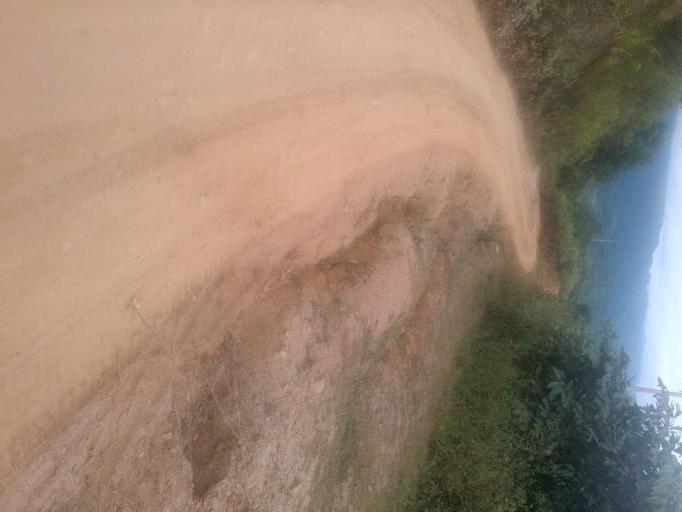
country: LA
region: Xiangkhoang
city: Muang Phonsavan
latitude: 19.3380
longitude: 103.5061
